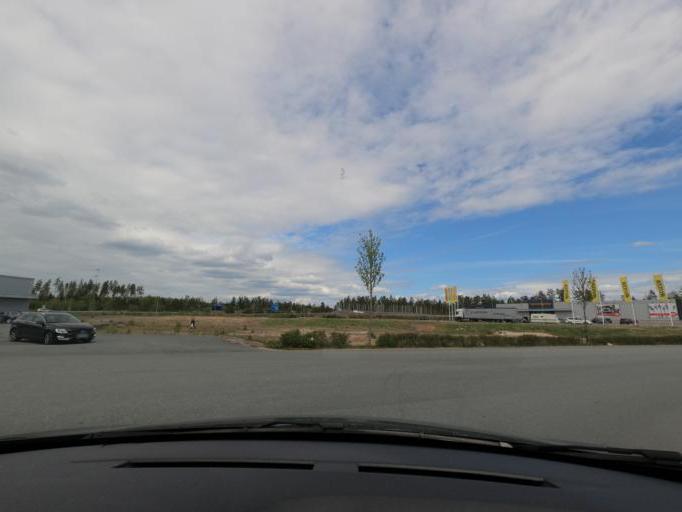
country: SE
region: Joenkoeping
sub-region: Gislaveds Kommun
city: Gislaved
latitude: 57.3214
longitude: 13.5447
